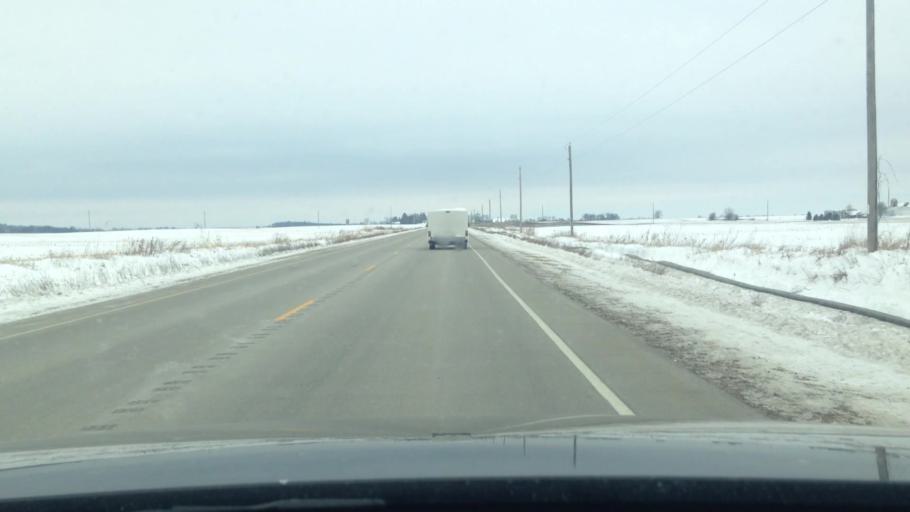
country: US
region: Illinois
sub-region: McHenry County
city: Hebron
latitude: 42.5096
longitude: -88.4426
